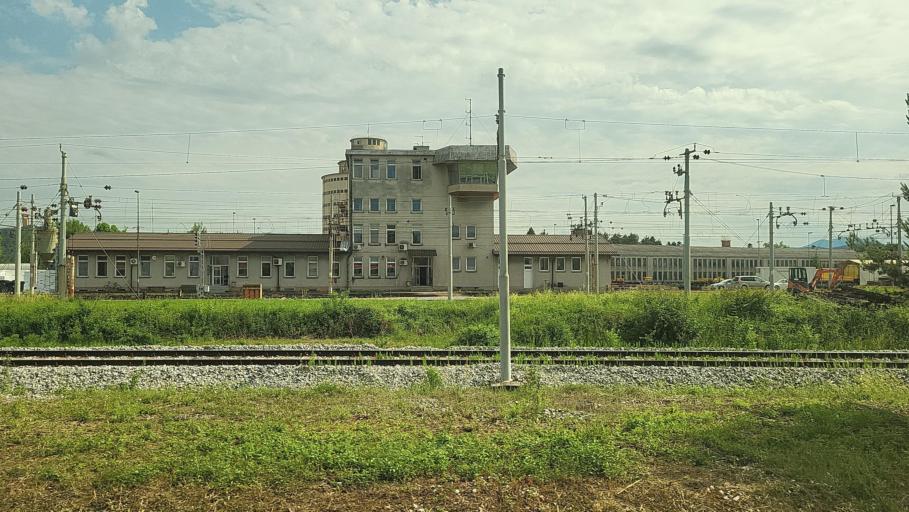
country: SI
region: Dol pri Ljubljani
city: Dol pri Ljubljani
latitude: 46.0597
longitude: 14.6065
